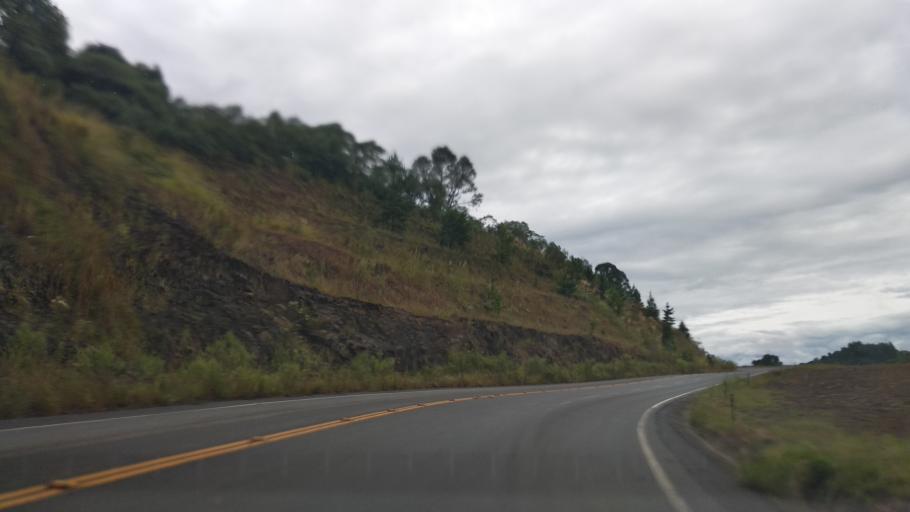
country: BR
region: Santa Catarina
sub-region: Videira
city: Videira
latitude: -27.0037
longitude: -51.1719
